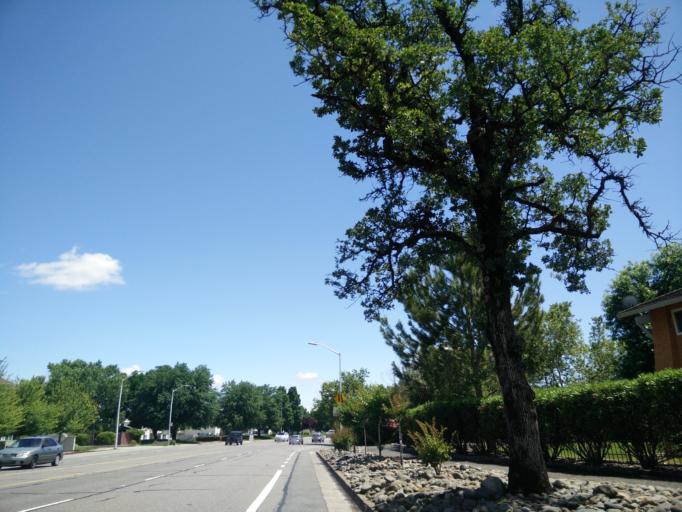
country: US
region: California
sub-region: Shasta County
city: Redding
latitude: 40.6005
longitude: -122.3726
